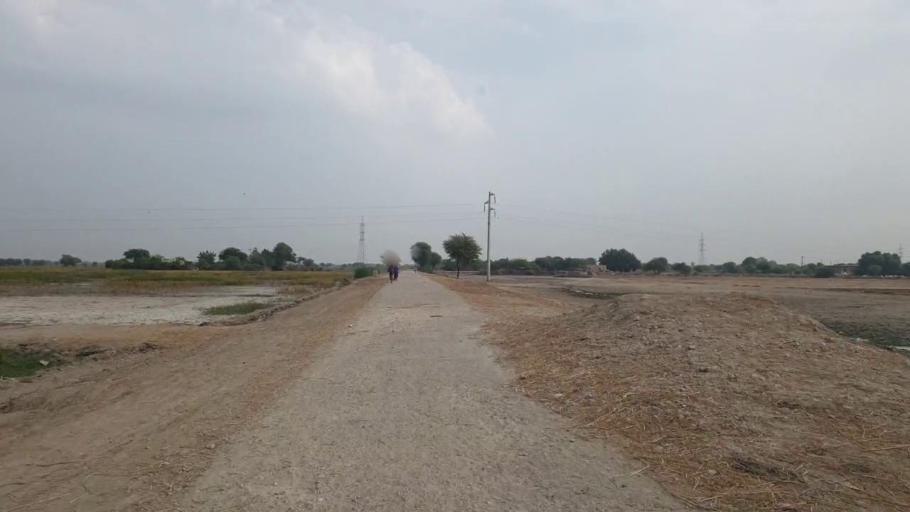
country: PK
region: Sindh
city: Matli
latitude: 24.9533
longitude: 68.6919
